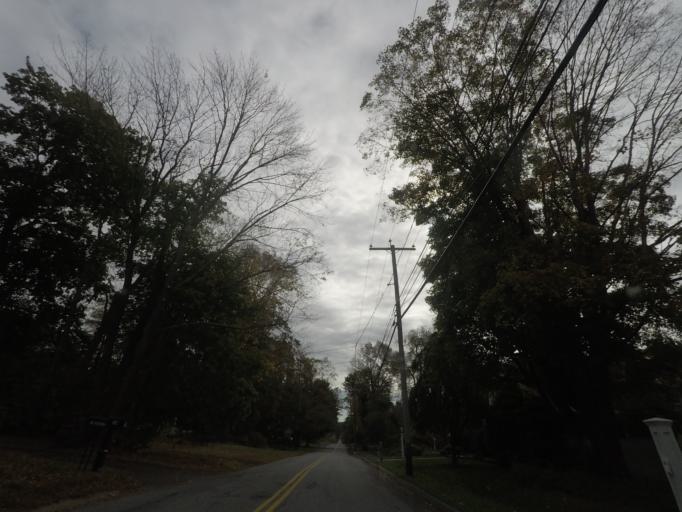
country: US
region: Connecticut
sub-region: Windham County
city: Thompson
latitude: 41.9580
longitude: -71.8615
